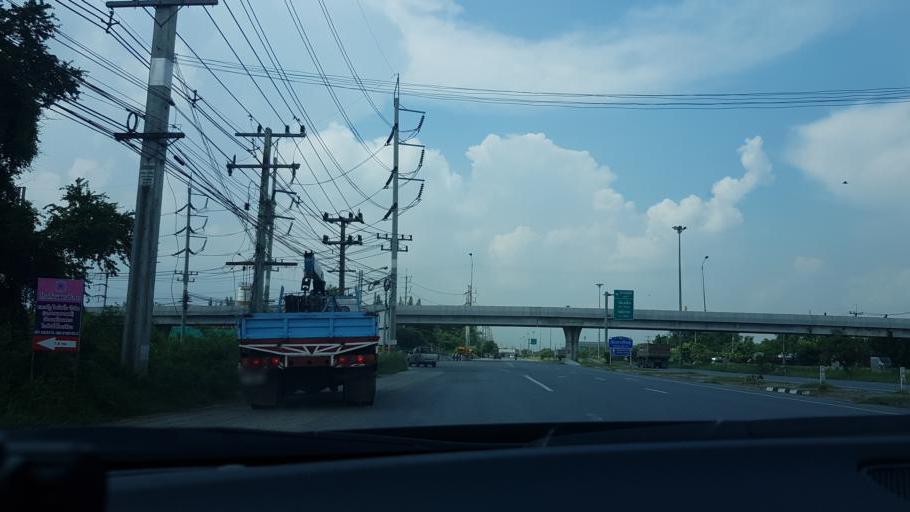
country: TH
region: Pathum Thani
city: Sam Khok
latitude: 14.0671
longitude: 100.5715
